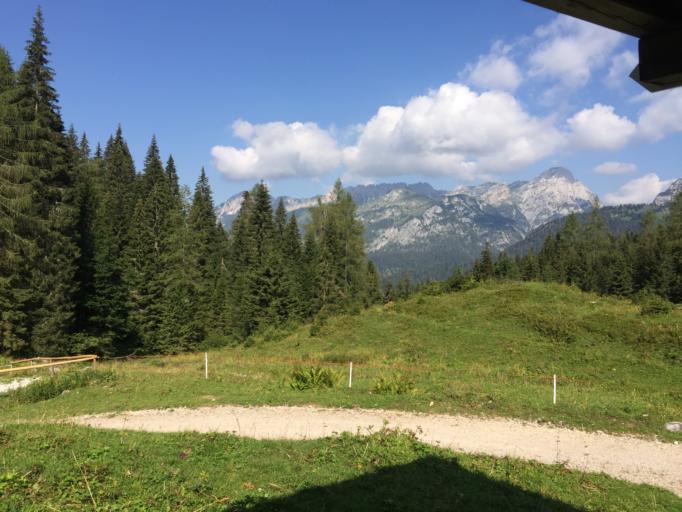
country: IT
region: Friuli Venezia Giulia
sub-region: Provincia di Udine
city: Forni Avoltri
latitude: 46.5610
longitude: 12.7593
